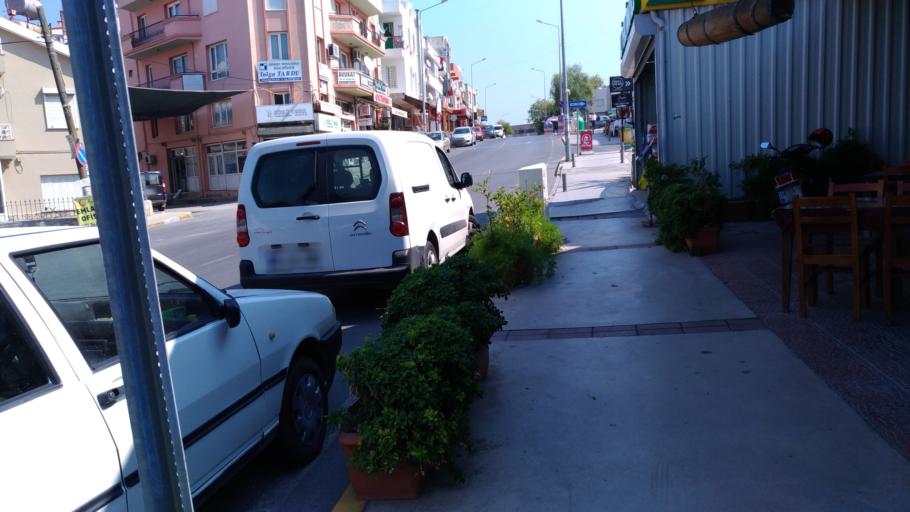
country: TR
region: Izmir
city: Urla
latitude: 38.3237
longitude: 26.7651
